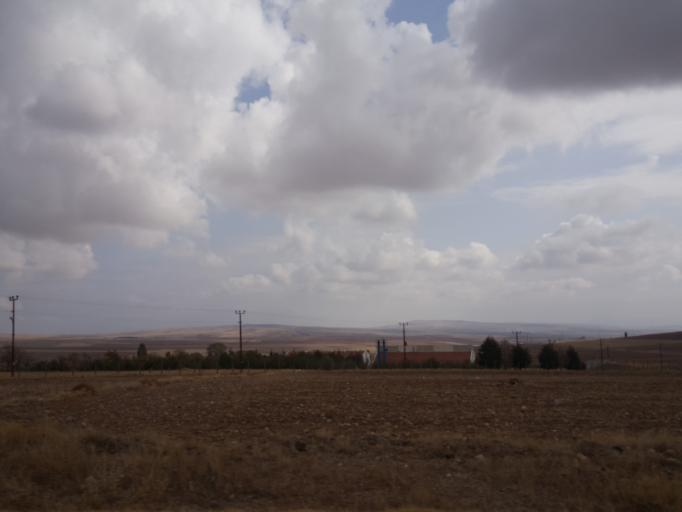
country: TR
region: Kirikkale
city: Keskin
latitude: 39.6453
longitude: 33.6191
